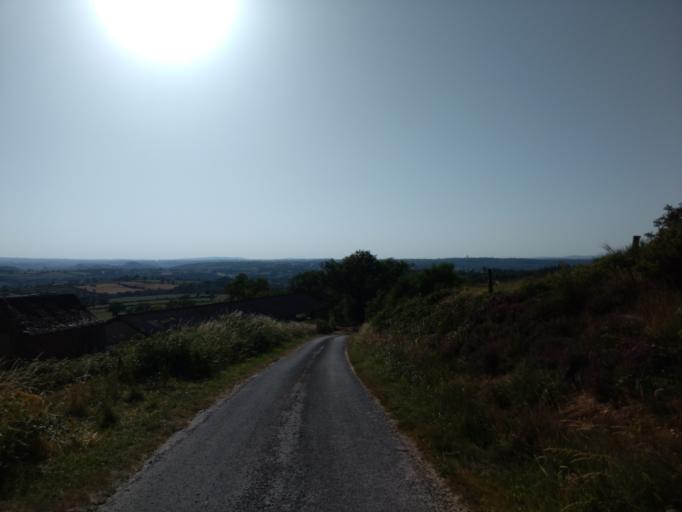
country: FR
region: Midi-Pyrenees
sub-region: Departement de l'Aveyron
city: La Loubiere
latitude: 44.3656
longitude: 2.6984
